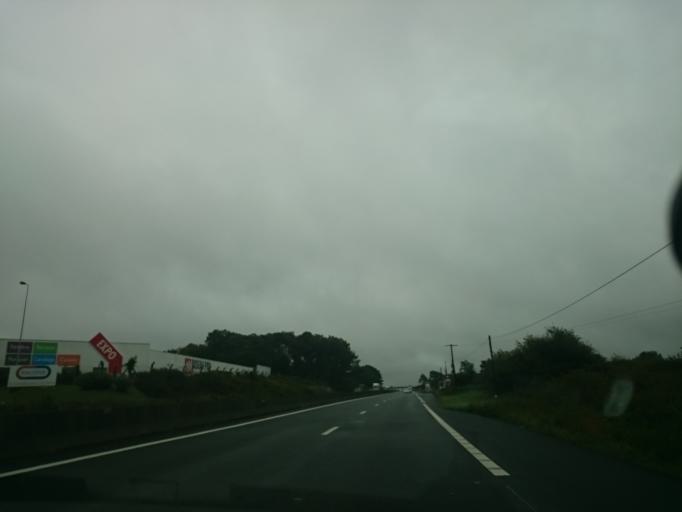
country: FR
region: Brittany
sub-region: Departement du Morbihan
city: Plougoumelen
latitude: 47.6659
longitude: -2.9070
